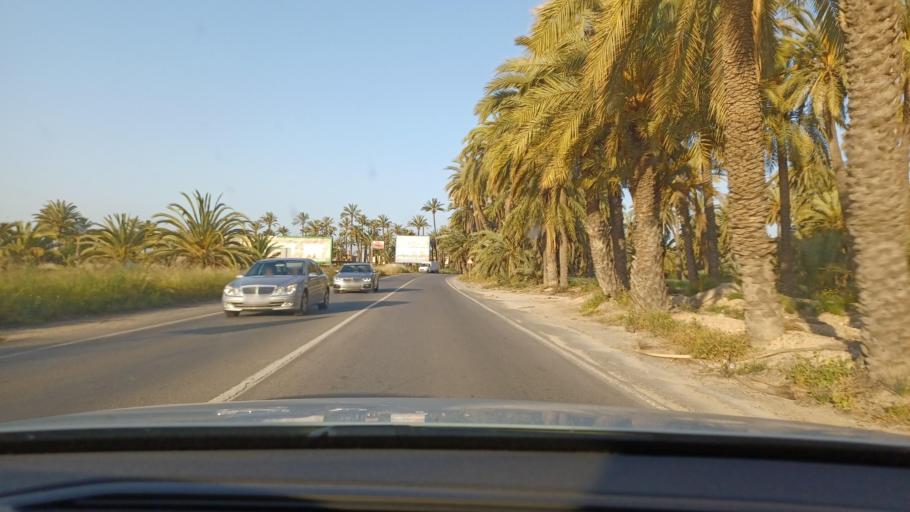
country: ES
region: Valencia
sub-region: Provincia de Alicante
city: Elche
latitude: 38.2579
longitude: -0.6846
